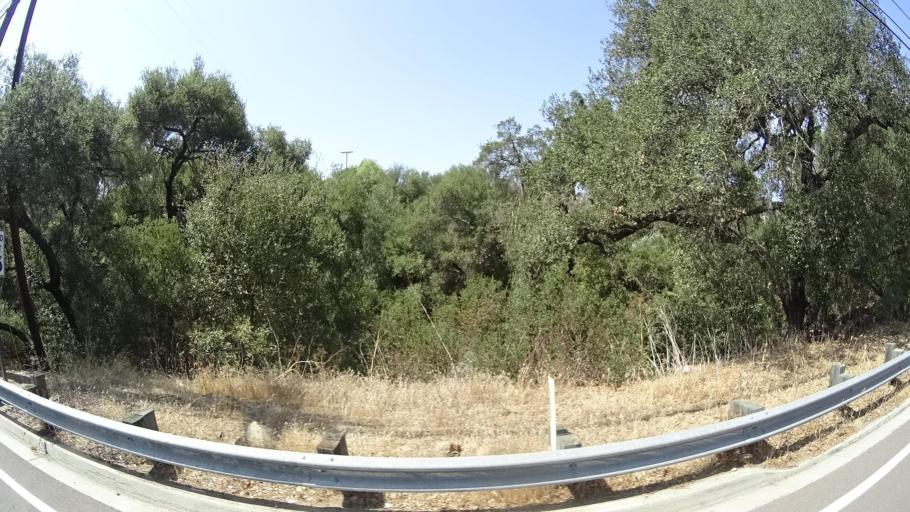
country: US
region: California
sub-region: San Diego County
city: Hidden Meadows
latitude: 33.1726
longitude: -117.1048
